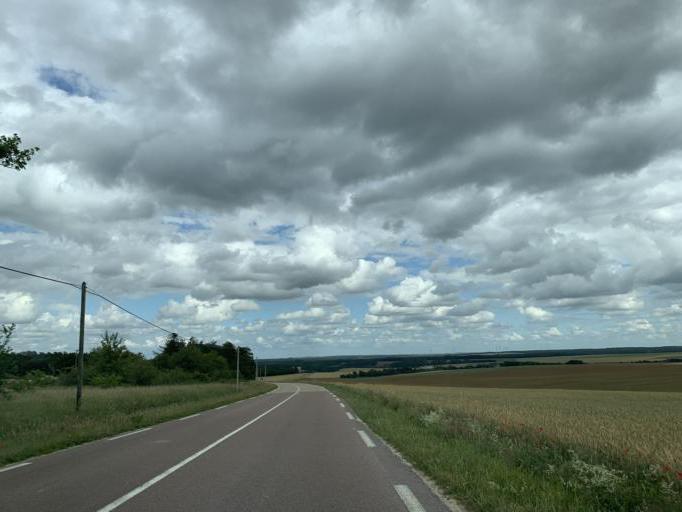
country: FR
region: Bourgogne
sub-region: Departement de l'Yonne
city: Vermenton
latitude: 47.7384
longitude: 3.7587
